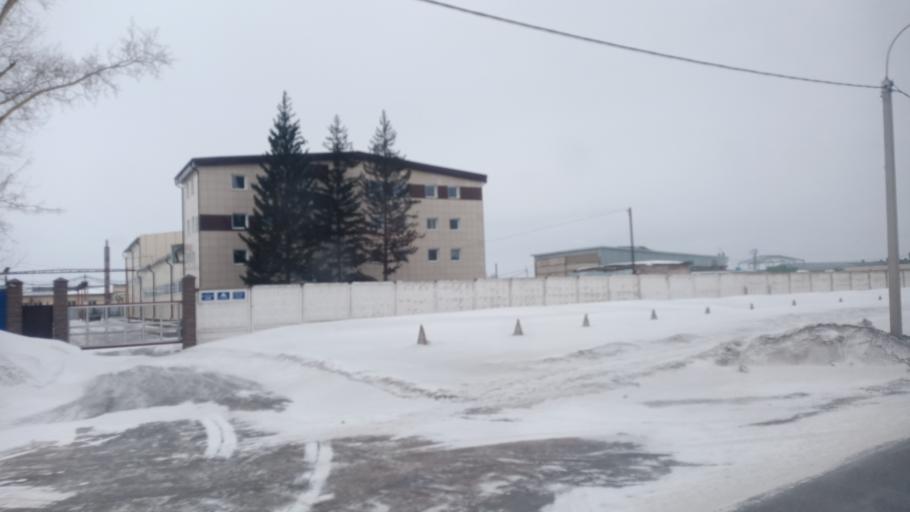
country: RU
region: Altai Krai
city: Novosilikatnyy
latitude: 53.3901
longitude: 83.6687
